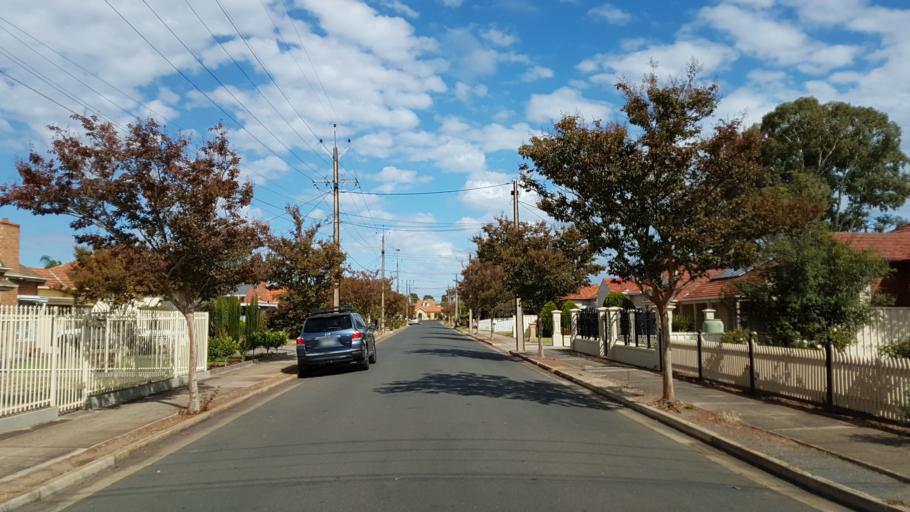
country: AU
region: South Australia
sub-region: City of West Torrens
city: Thebarton
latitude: -34.9268
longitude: 138.5463
